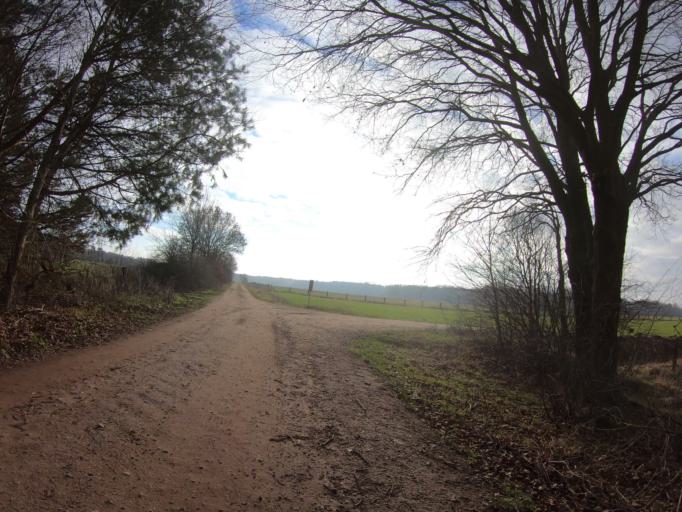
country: DE
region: Lower Saxony
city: Ribbesbuttel
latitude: 52.4820
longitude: 10.4841
